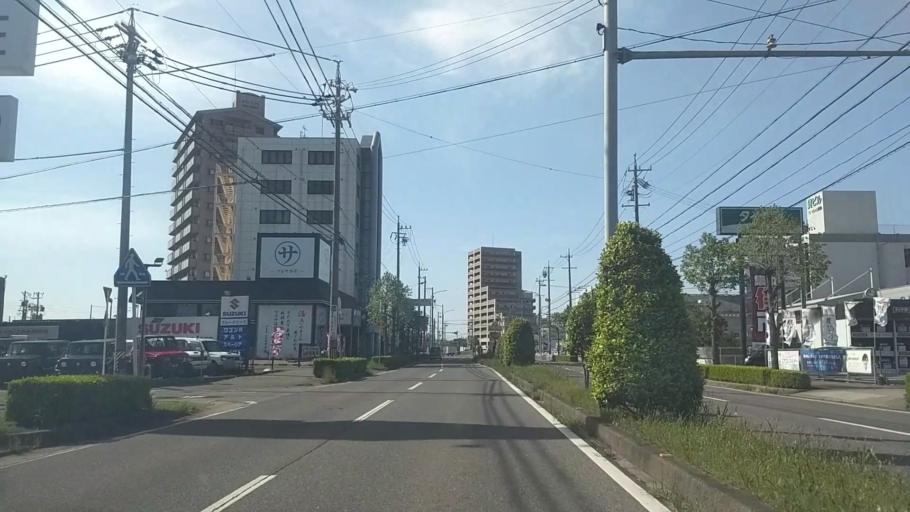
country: JP
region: Aichi
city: Anjo
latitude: 34.9675
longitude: 137.0568
